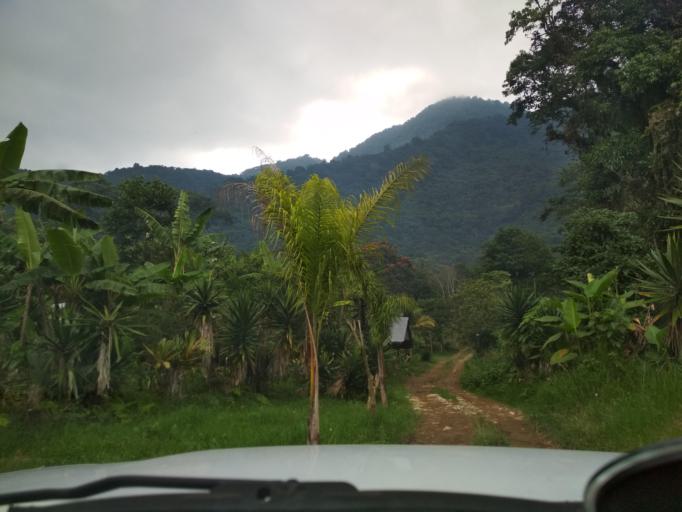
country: MX
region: Veracruz
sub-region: Fortin
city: Santa Lucia Potrerillo
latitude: 18.9566
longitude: -97.0492
